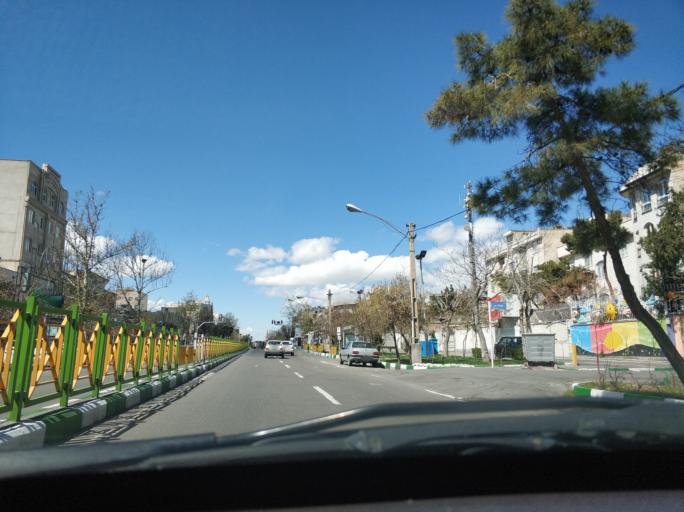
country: IR
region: Tehran
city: Tehran
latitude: 35.7202
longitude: 51.4933
